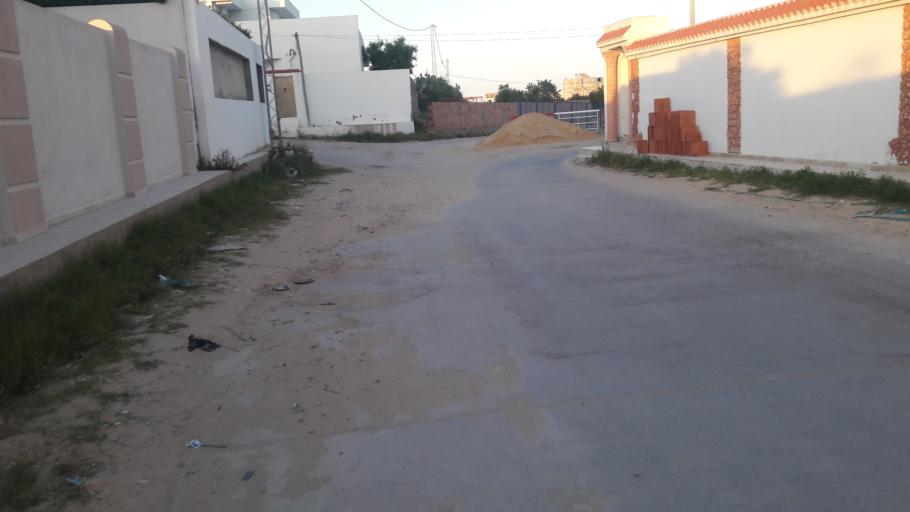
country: TN
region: Safaqis
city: Sfax
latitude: 34.8084
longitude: 10.7451
